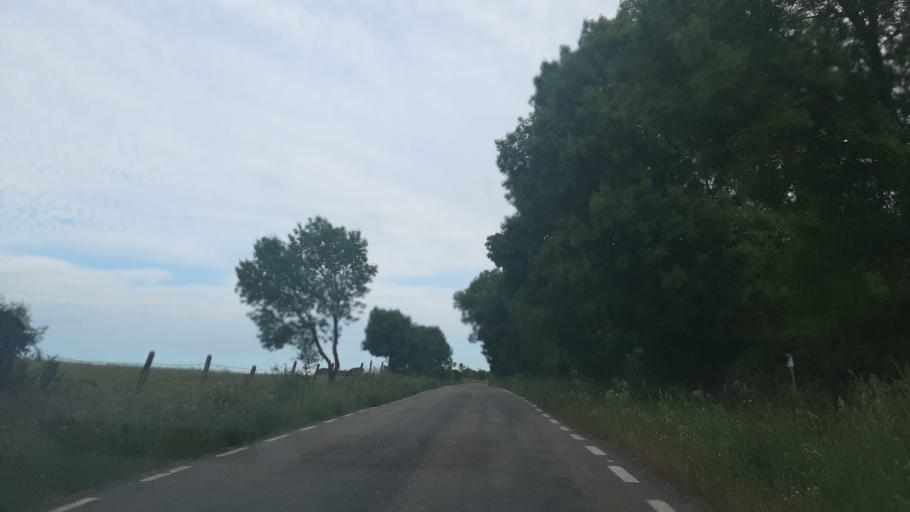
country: ES
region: Castille and Leon
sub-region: Provincia de Salamanca
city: Gallegos de Arganan
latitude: 40.6389
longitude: -6.7286
